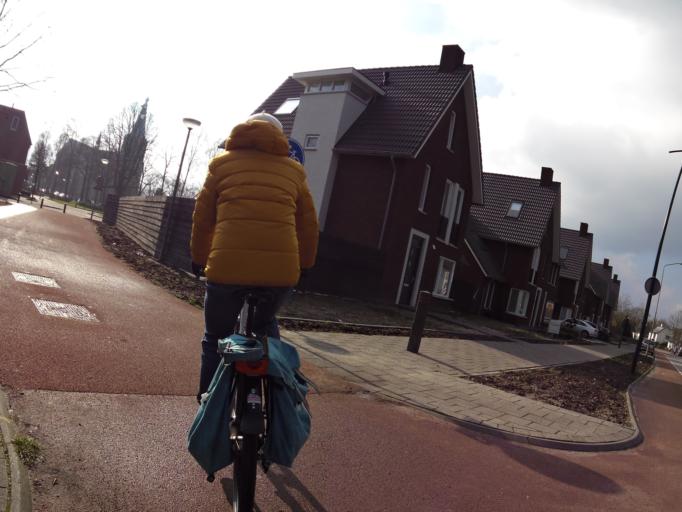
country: NL
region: North Brabant
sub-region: Gemeente Boxtel
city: Boxtel
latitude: 51.5915
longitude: 5.3293
